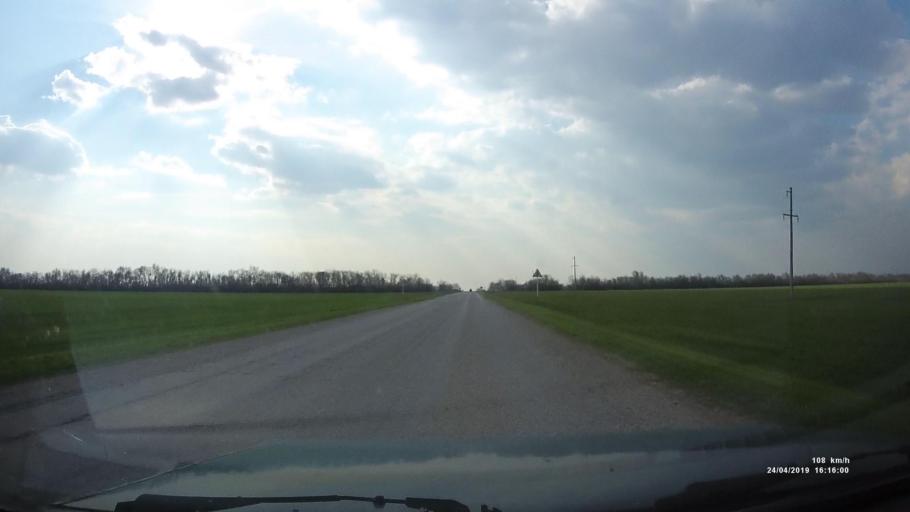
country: RU
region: Rostov
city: Sovetskoye
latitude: 46.7607
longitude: 42.1687
